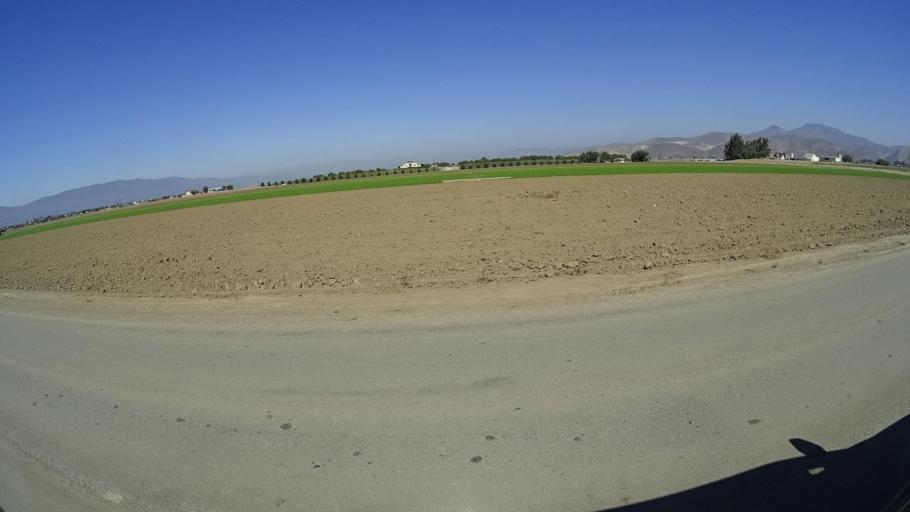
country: US
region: California
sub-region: Monterey County
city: Greenfield
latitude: 36.3311
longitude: -121.2167
